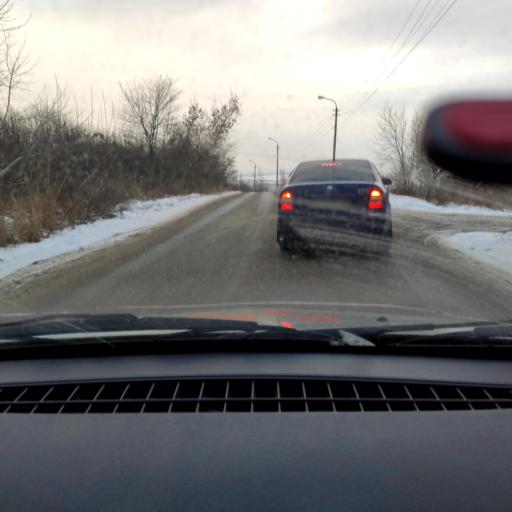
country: RU
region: Bashkortostan
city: Blagoveshchensk
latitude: 54.8918
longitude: 56.0510
